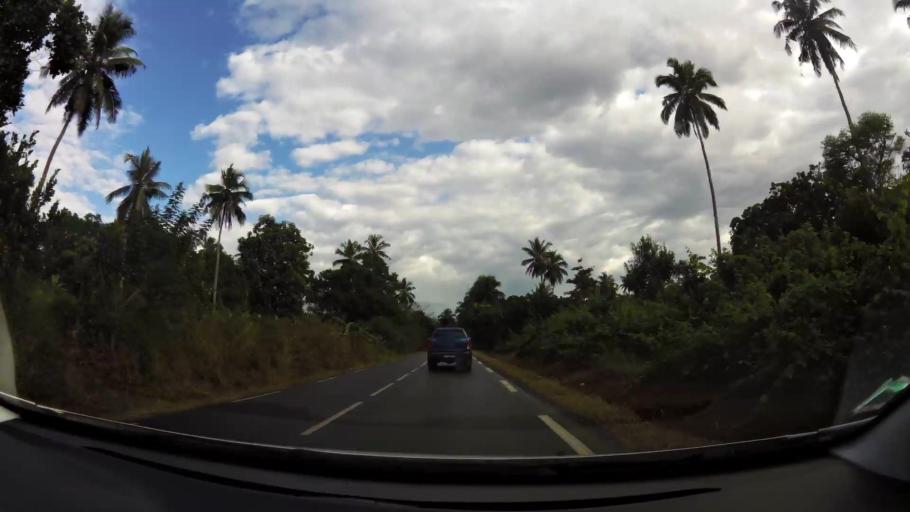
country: YT
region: Ouangani
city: Ouangani
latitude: -12.8351
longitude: 45.1417
